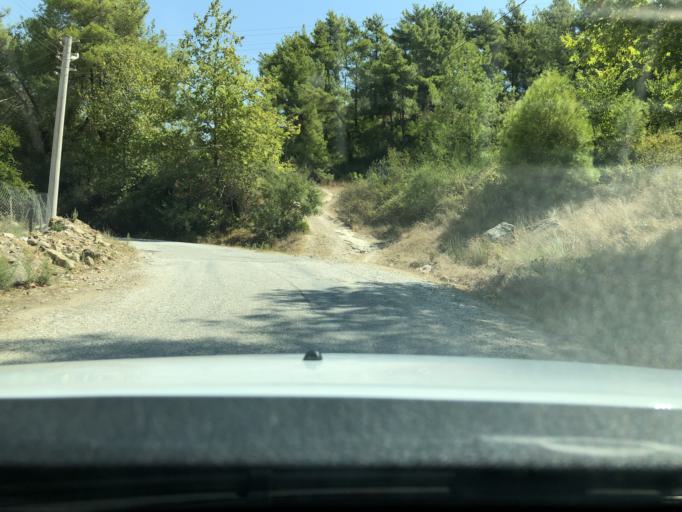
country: TR
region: Antalya
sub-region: Manavgat
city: Manavgat
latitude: 36.8341
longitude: 31.5235
